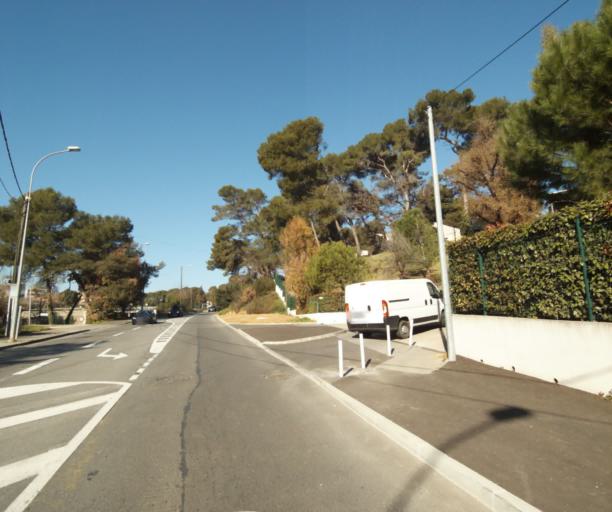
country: FR
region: Provence-Alpes-Cote d'Azur
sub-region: Departement des Alpes-Maritimes
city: Biot
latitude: 43.5995
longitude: 7.1004
